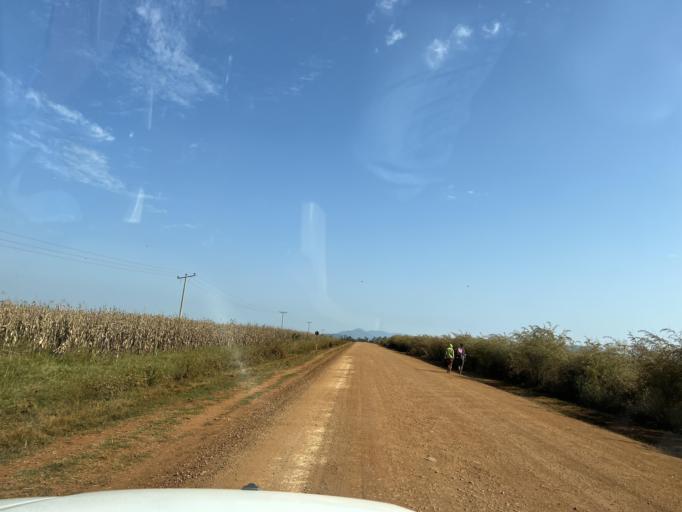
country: ET
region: Oromiya
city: Shambu
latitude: 9.4076
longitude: 36.5398
